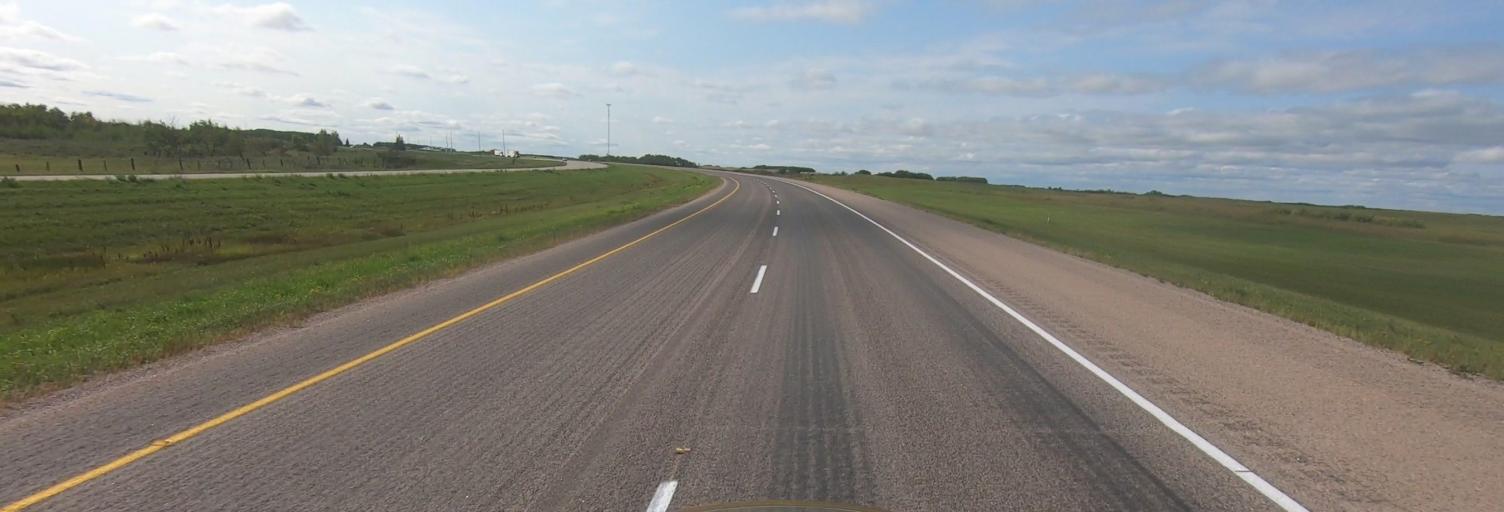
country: CA
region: Saskatchewan
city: Moosomin
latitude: 50.0278
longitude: -101.3574
